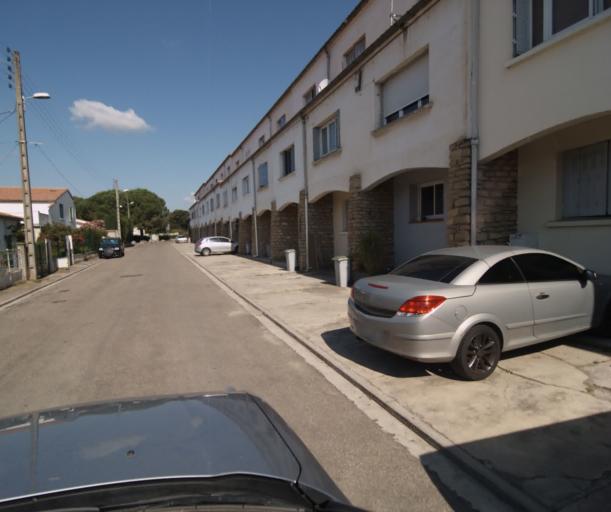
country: FR
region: Languedoc-Roussillon
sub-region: Departement de l'Aude
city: Limoux
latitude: 43.0669
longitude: 2.2192
